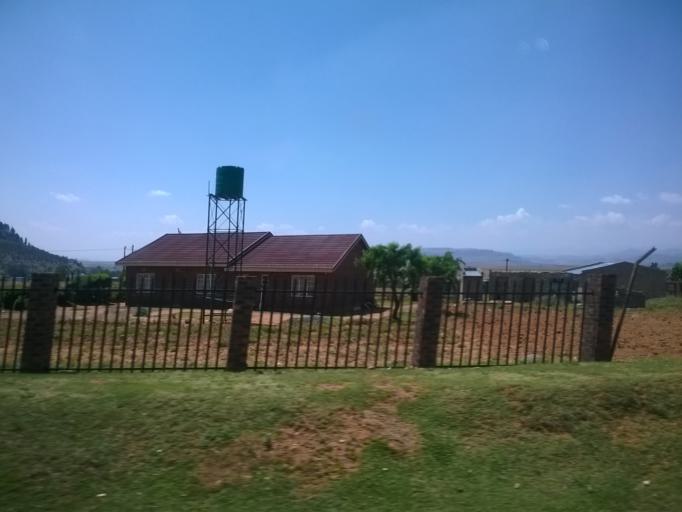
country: LS
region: Leribe
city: Maputsoe
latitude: -28.9604
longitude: 27.9614
